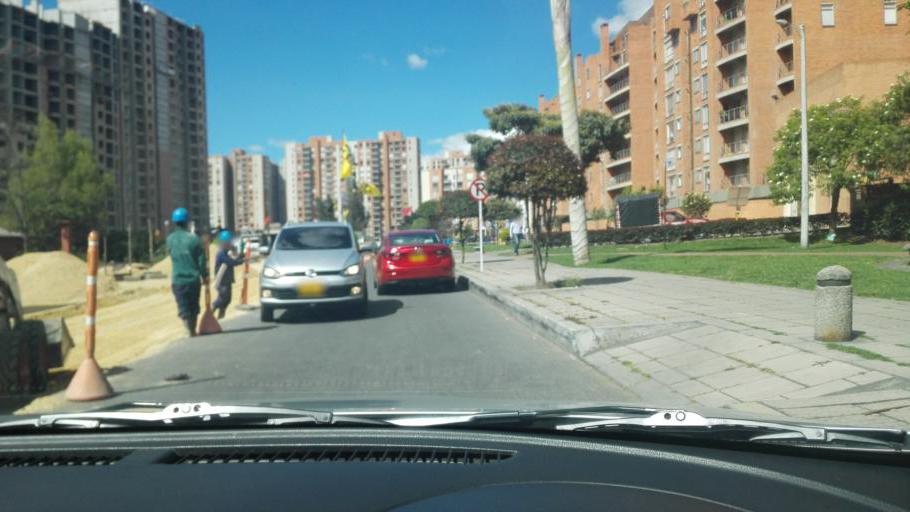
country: CO
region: Cundinamarca
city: Cota
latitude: 4.7404
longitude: -74.0670
